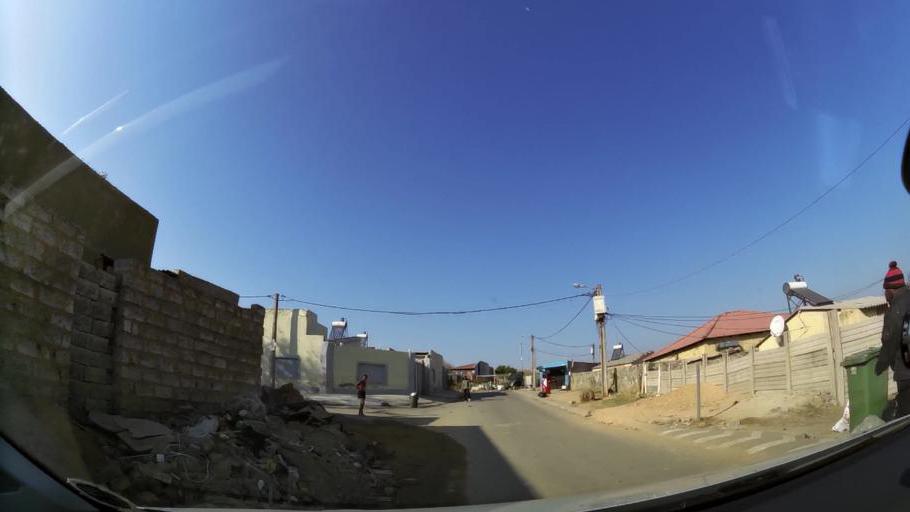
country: ZA
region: Gauteng
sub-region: City of Johannesburg Metropolitan Municipality
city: Modderfontein
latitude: -26.0901
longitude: 28.1134
